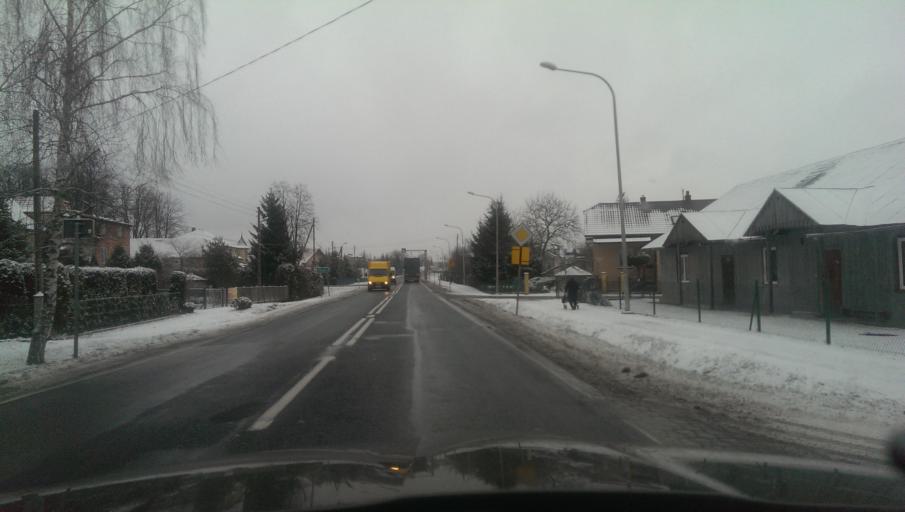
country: PL
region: Subcarpathian Voivodeship
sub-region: Powiat sanocki
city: Dlugie
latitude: 49.5783
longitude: 22.0423
